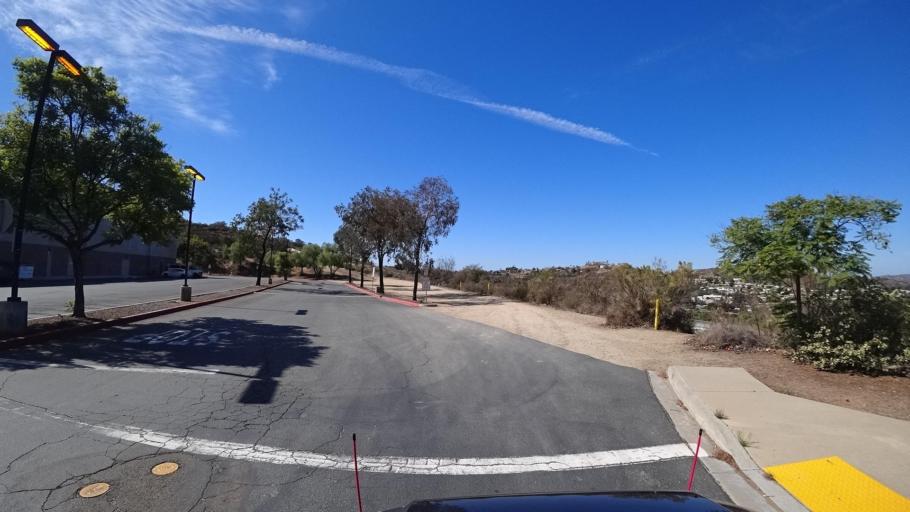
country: US
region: California
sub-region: San Diego County
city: Granite Hills
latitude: 32.8250
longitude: -116.9040
